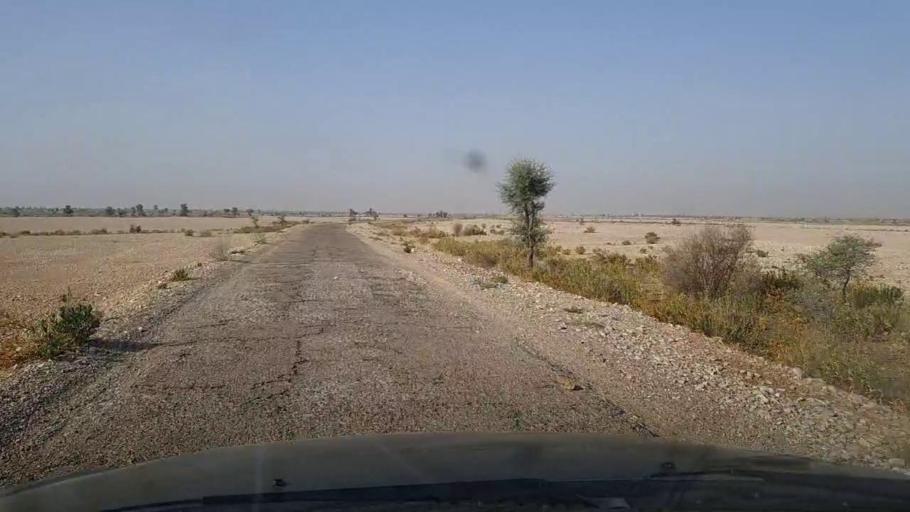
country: PK
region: Sindh
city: Sann
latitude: 25.9936
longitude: 68.0718
